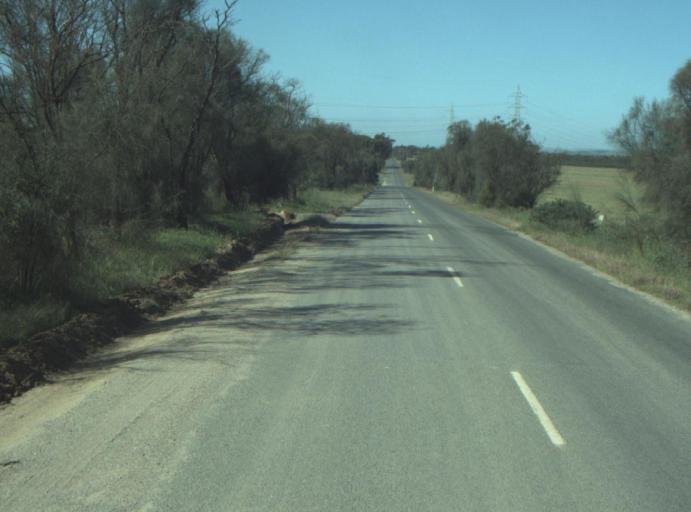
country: AU
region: Victoria
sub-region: Greater Geelong
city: Lara
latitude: -37.9263
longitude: 144.3954
